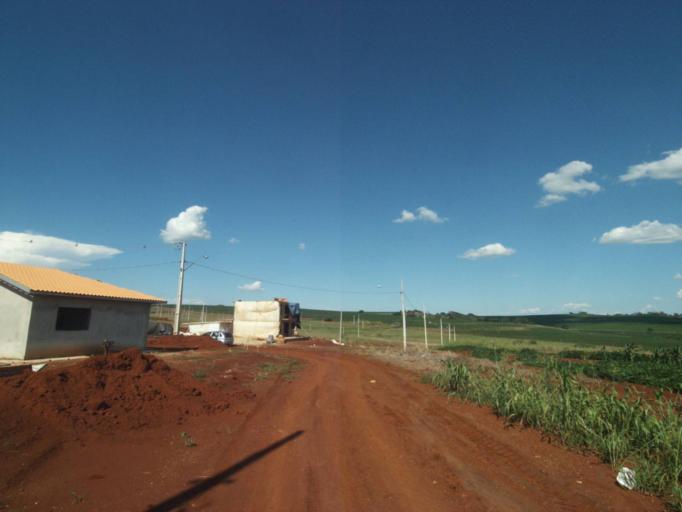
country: BR
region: Parana
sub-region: Sertanopolis
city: Sertanopolis
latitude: -23.0481
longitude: -50.8178
